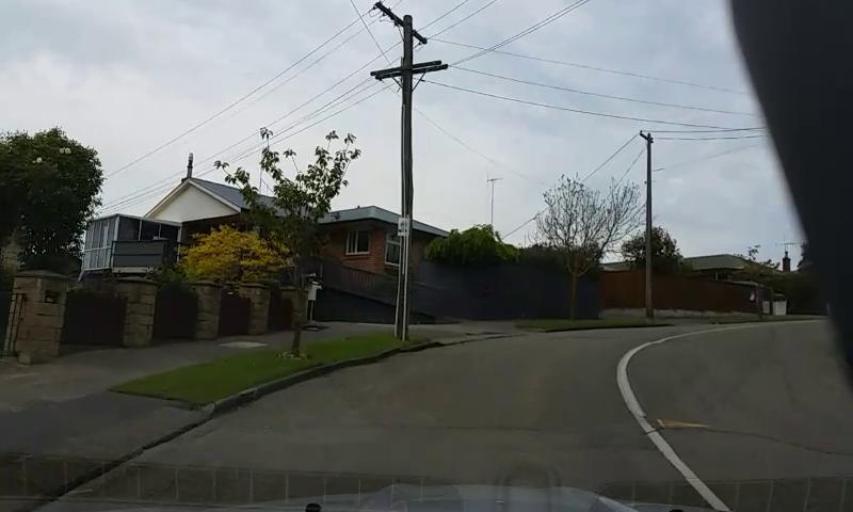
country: NZ
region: Canterbury
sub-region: Timaru District
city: Timaru
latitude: -44.3734
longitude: 171.2342
